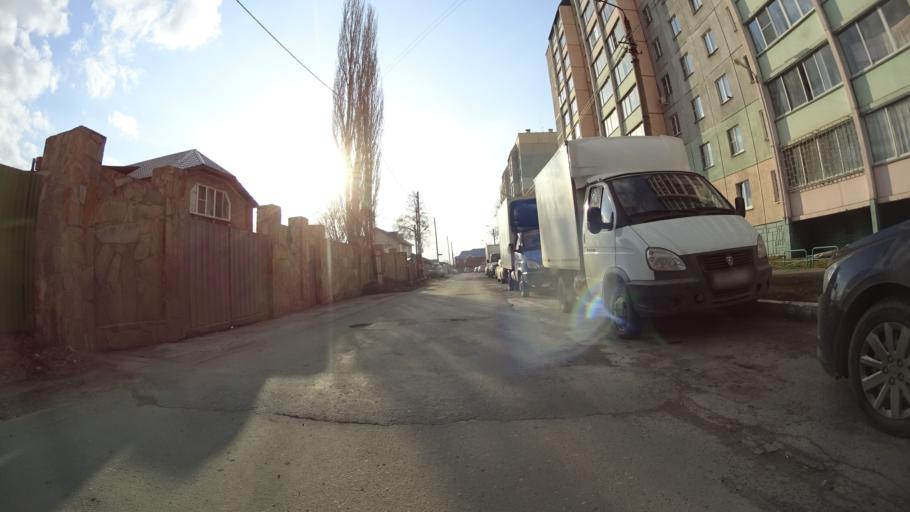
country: RU
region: Chelyabinsk
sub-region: Gorod Chelyabinsk
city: Chelyabinsk
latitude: 55.1366
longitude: 61.3984
